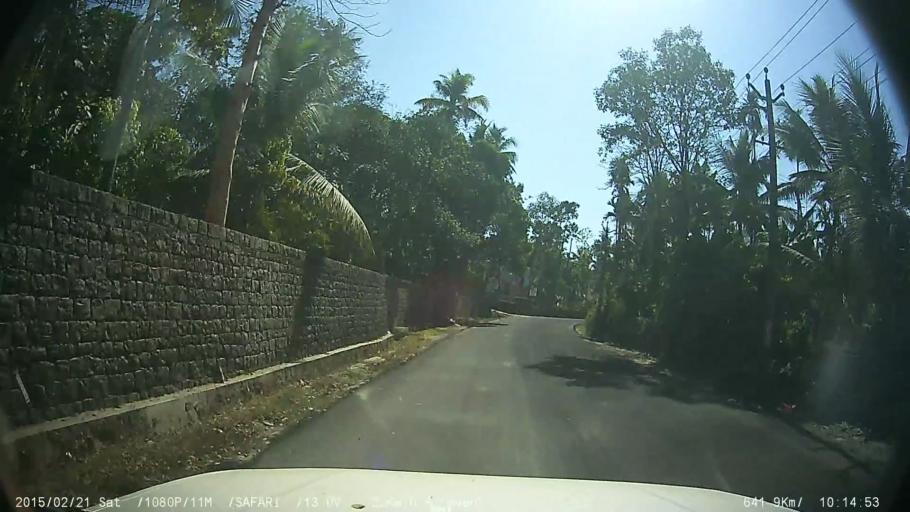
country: IN
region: Kerala
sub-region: Ernakulam
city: Muvattupuzha
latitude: 9.8857
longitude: 76.6396
